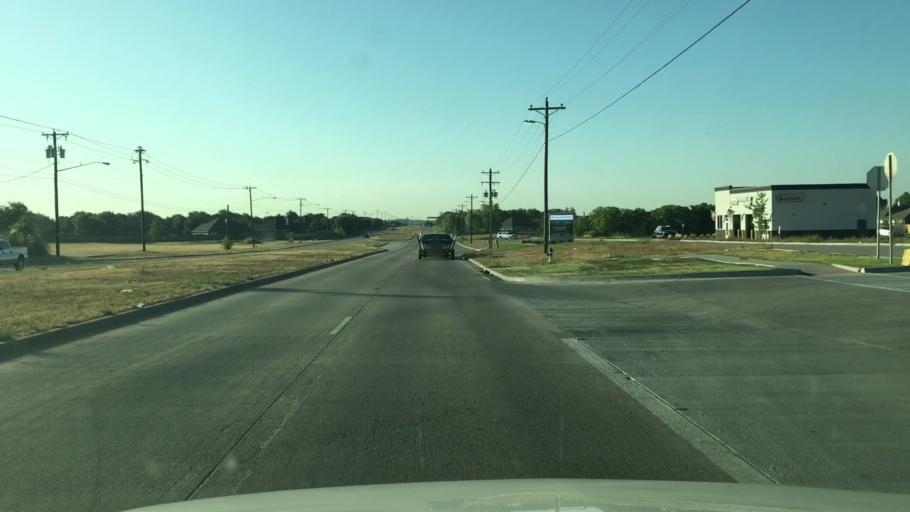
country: US
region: Texas
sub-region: Johnson County
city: Burleson
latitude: 32.5384
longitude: -97.3603
